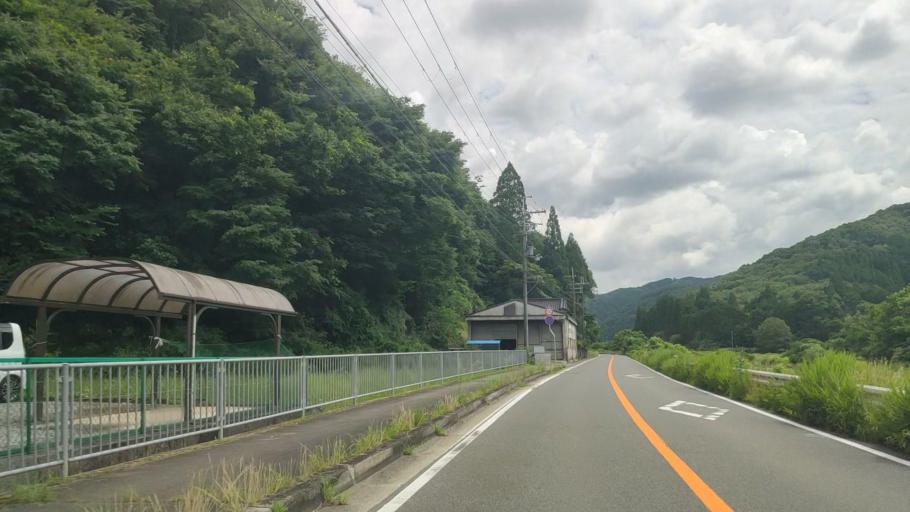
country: JP
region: Hyogo
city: Yamazakicho-nakabirose
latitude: 34.9727
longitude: 134.4467
